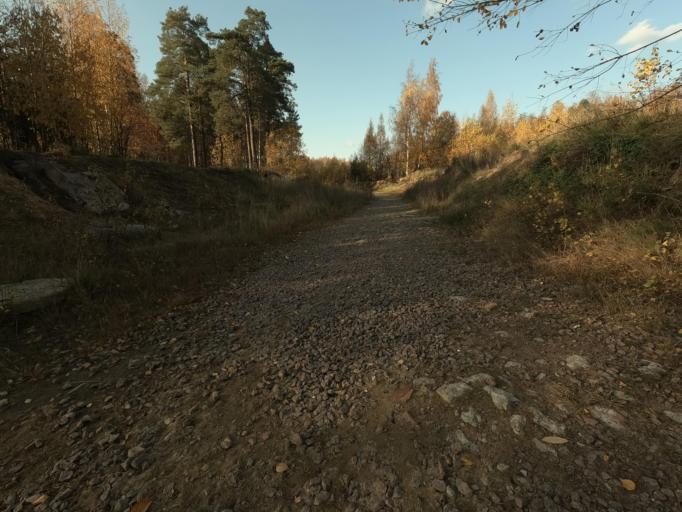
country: RU
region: Leningrad
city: Sertolovo
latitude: 60.1510
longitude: 30.2217
